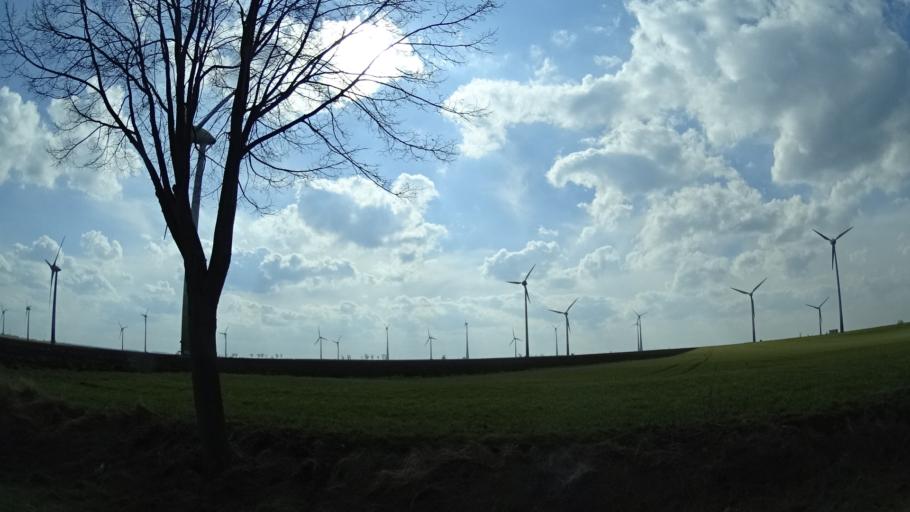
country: DE
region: Saxony-Anhalt
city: Stossen
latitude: 51.1059
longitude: 11.9343
